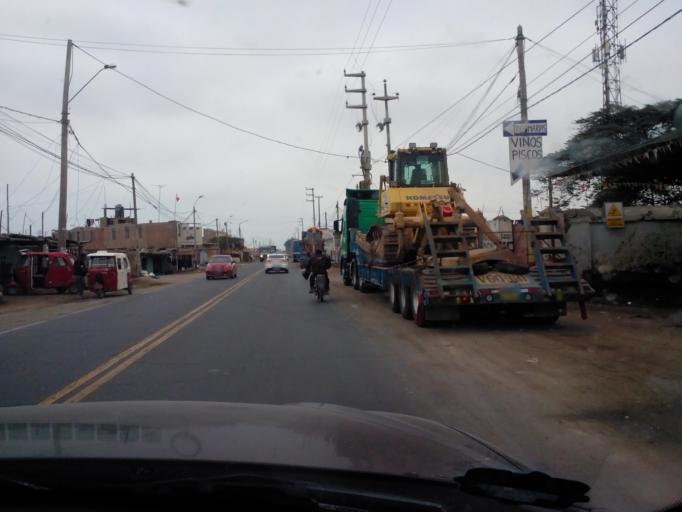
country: PE
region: Ica
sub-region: Provincia de Chincha
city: San Pedro
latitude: -13.4134
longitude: -76.1513
